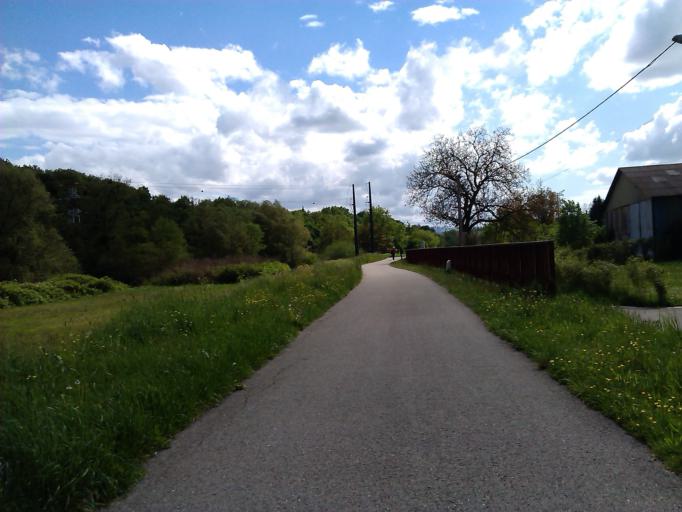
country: FR
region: Franche-Comte
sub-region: Departement du Doubs
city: Bart
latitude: 47.4892
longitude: 6.7730
